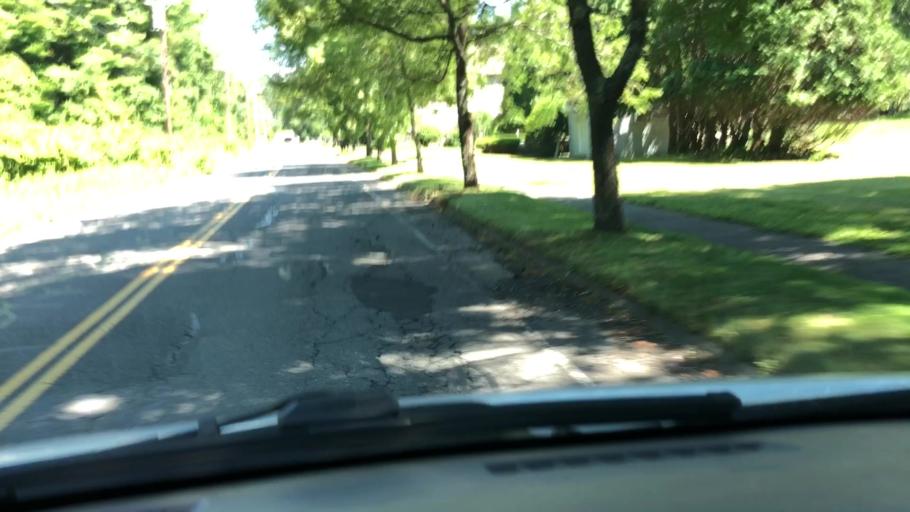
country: US
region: Massachusetts
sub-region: Hampshire County
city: Northampton
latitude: 42.3277
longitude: -72.6567
